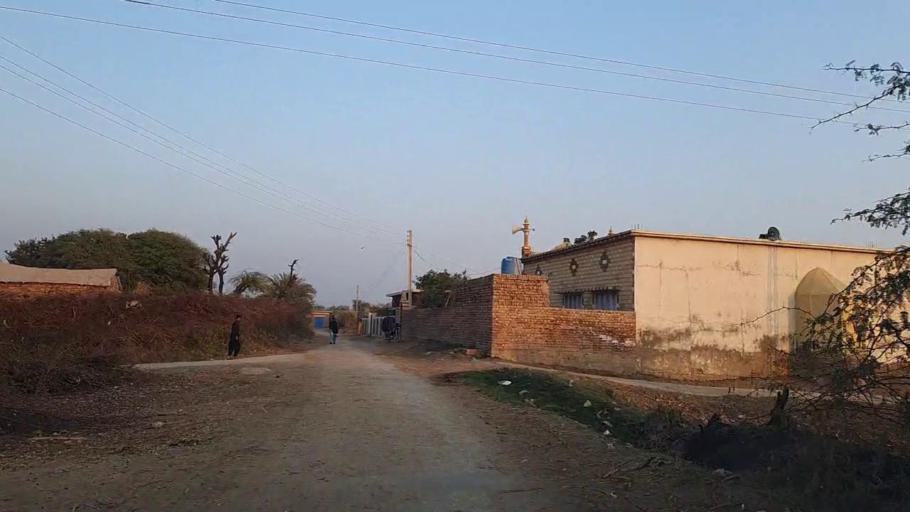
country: PK
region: Sindh
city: Jam Sahib
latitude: 26.3059
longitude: 68.5474
